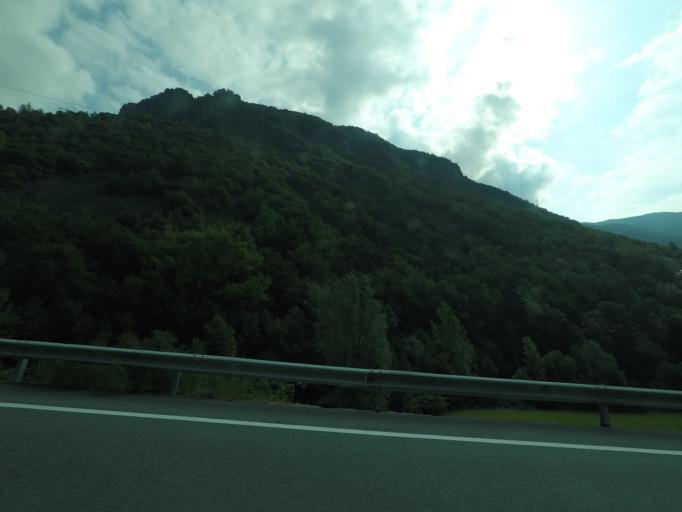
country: IT
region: Aosta Valley
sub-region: Valle d'Aosta
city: Antey-Saint-Andre
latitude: 45.7803
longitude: 7.5910
